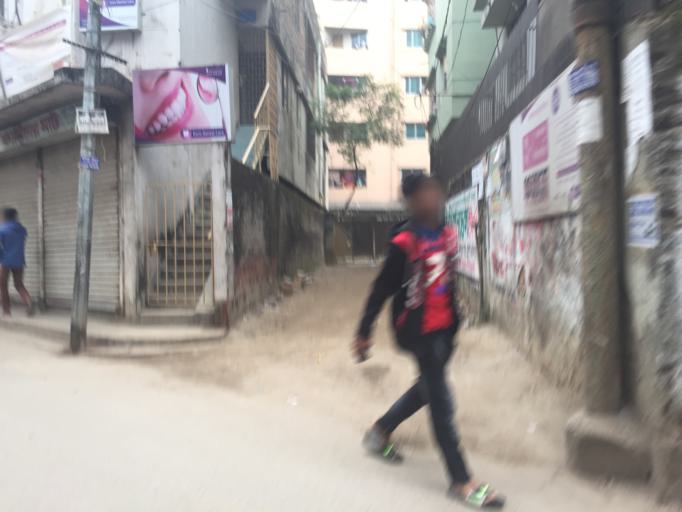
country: BD
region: Dhaka
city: Azimpur
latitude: 23.7843
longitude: 90.3597
